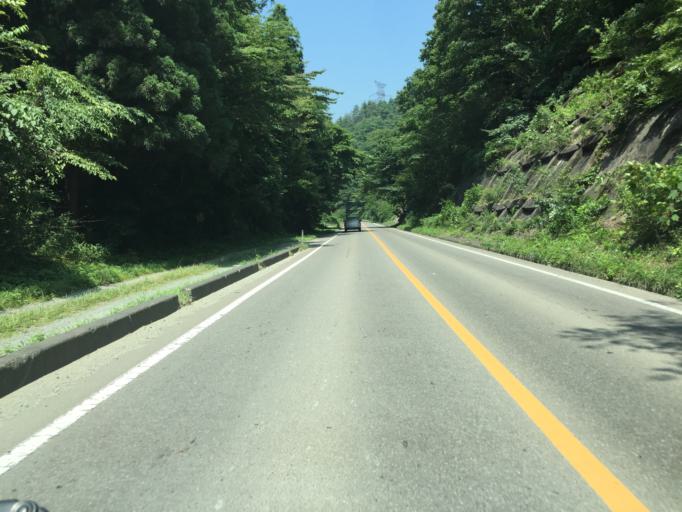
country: JP
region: Miyagi
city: Marumori
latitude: 37.8524
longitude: 140.8527
